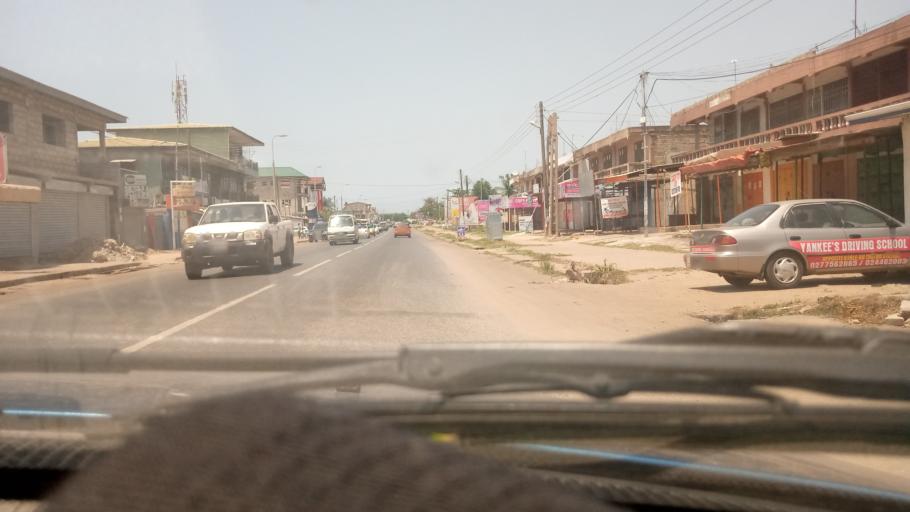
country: GH
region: Greater Accra
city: Accra
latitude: 5.5353
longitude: -0.2309
